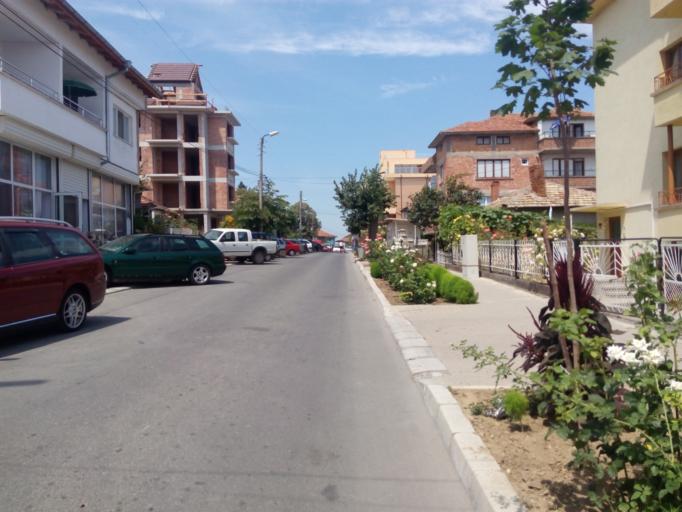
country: BG
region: Burgas
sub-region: Obshtina Nesebur
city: Obzor
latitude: 42.8184
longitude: 27.8835
